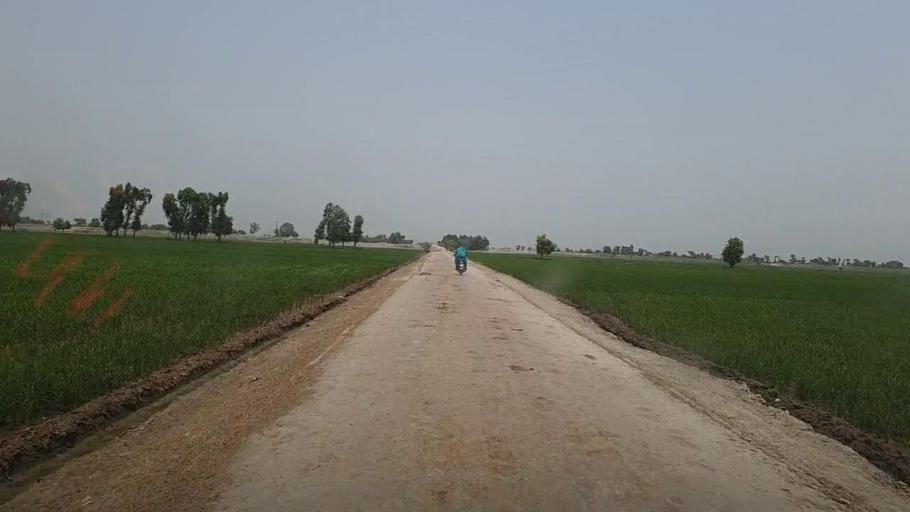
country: PK
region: Sindh
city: Sita Road
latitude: 27.0459
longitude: 67.8469
